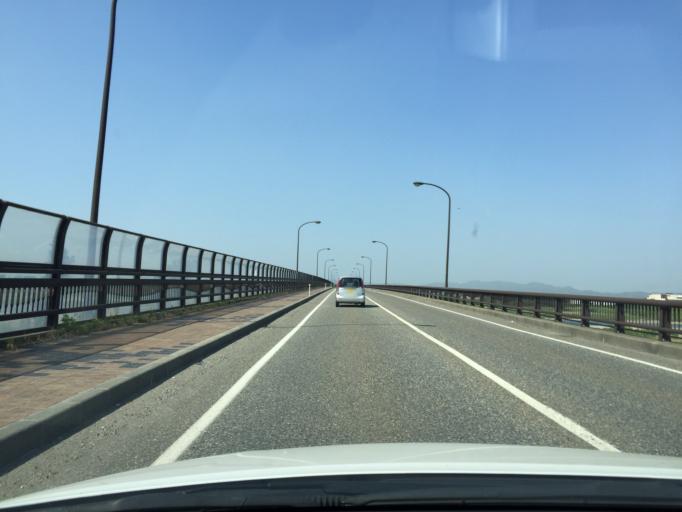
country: JP
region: Niigata
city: Gosen
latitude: 37.7535
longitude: 139.2266
